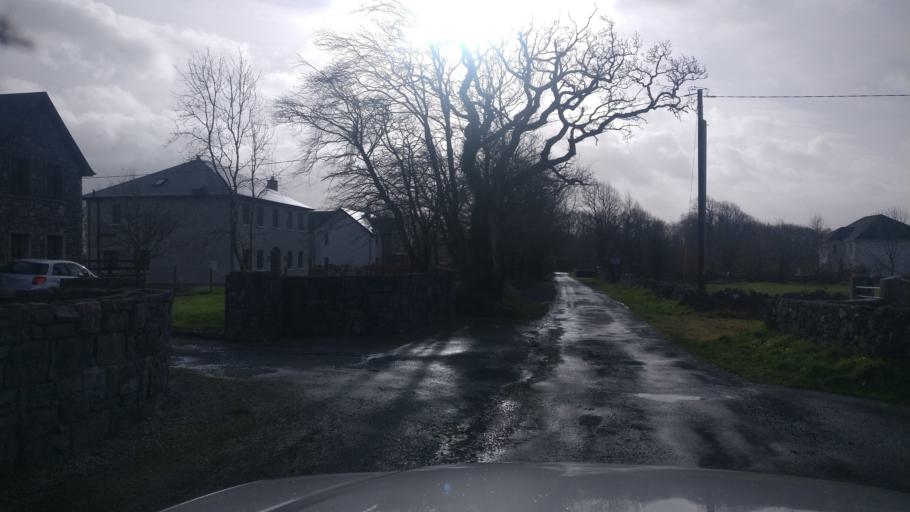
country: IE
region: Connaught
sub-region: County Galway
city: Loughrea
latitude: 53.2853
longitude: -8.5954
